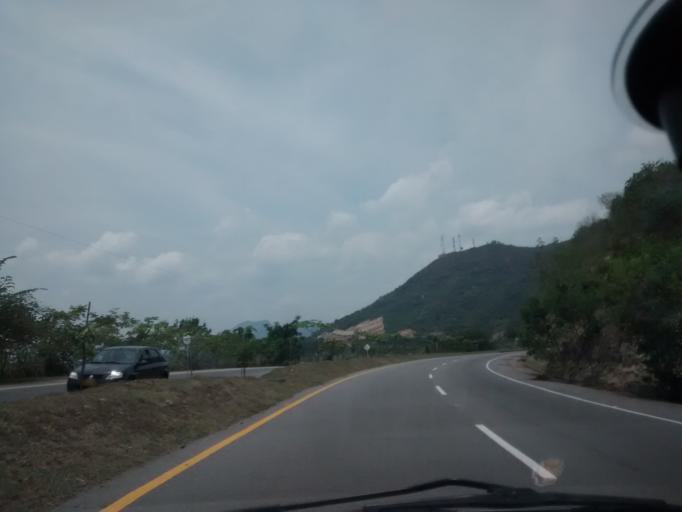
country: CO
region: Tolima
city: Espinal
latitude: 4.2172
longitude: -74.9638
